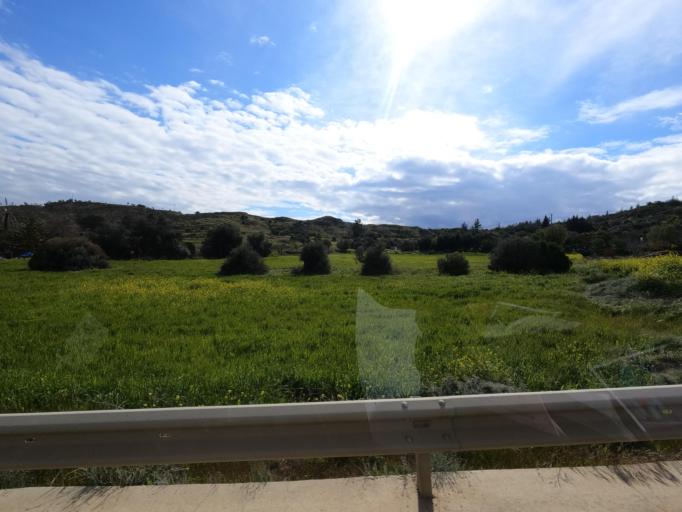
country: CY
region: Lefkosia
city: Lefka
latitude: 35.0842
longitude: 32.8887
